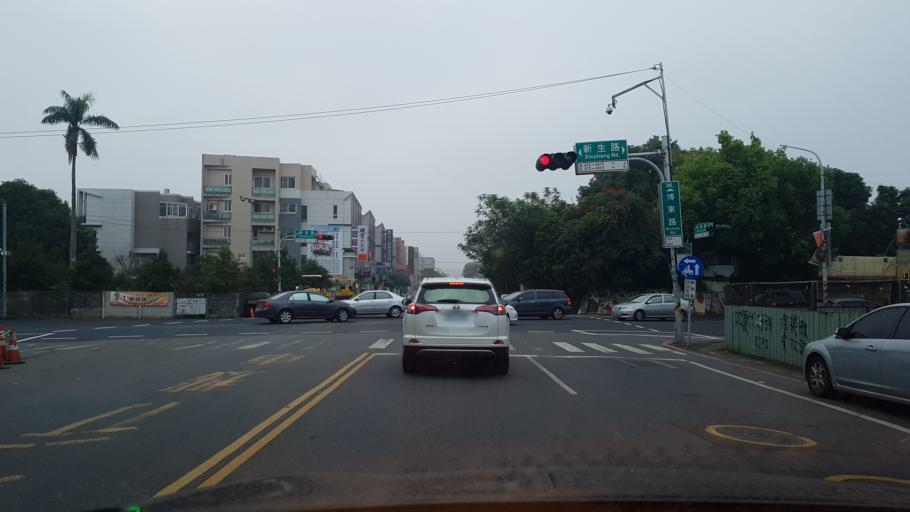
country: TW
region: Taiwan
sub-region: Chiayi
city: Jiayi Shi
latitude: 23.4908
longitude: 120.4591
